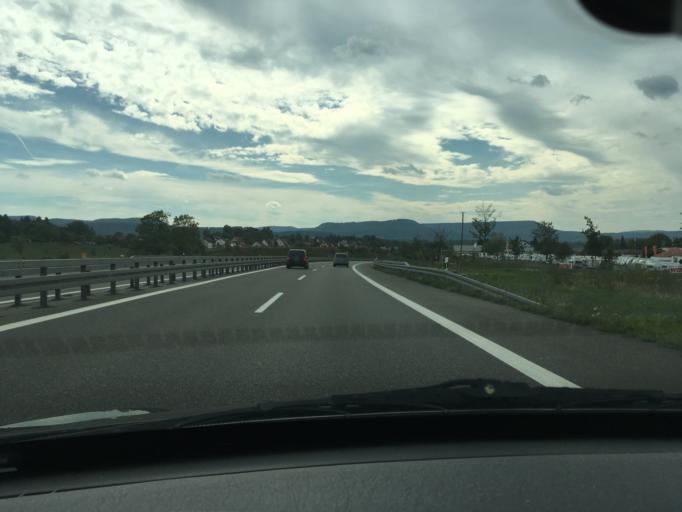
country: DE
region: Baden-Wuerttemberg
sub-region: Tuebingen Region
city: Dusslingen
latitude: 48.4584
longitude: 9.0620
